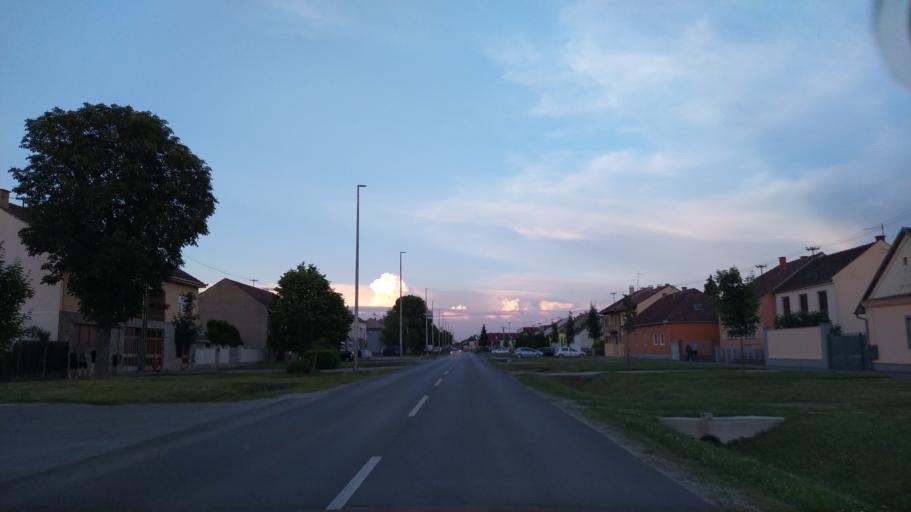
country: HR
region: Osjecko-Baranjska
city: Cepin
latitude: 45.5236
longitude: 18.5716
